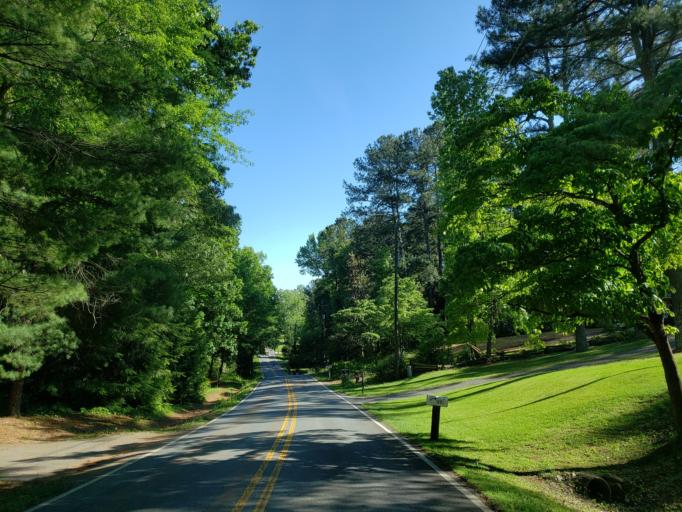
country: US
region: Georgia
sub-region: Paulding County
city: Hiram
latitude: 33.9057
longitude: -84.7937
